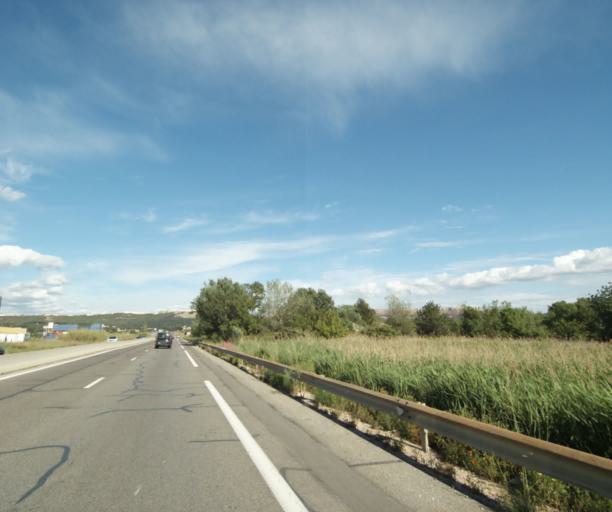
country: FR
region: Provence-Alpes-Cote d'Azur
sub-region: Departement des Bouches-du-Rhone
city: Rognac
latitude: 43.4934
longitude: 5.2115
